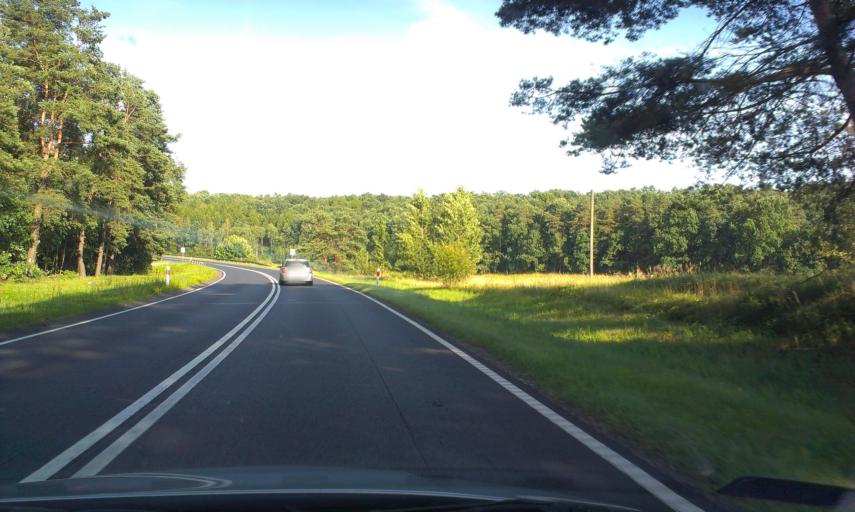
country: PL
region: Kujawsko-Pomorskie
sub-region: Powiat bydgoski
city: Sicienko
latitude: 53.1603
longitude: 17.7944
